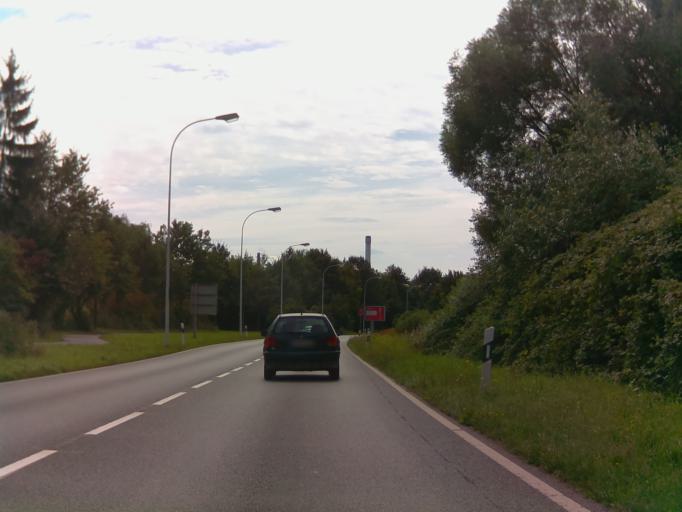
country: DE
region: Hesse
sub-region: Regierungsbezirk Darmstadt
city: Darmstadt
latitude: 49.8917
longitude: 8.6602
